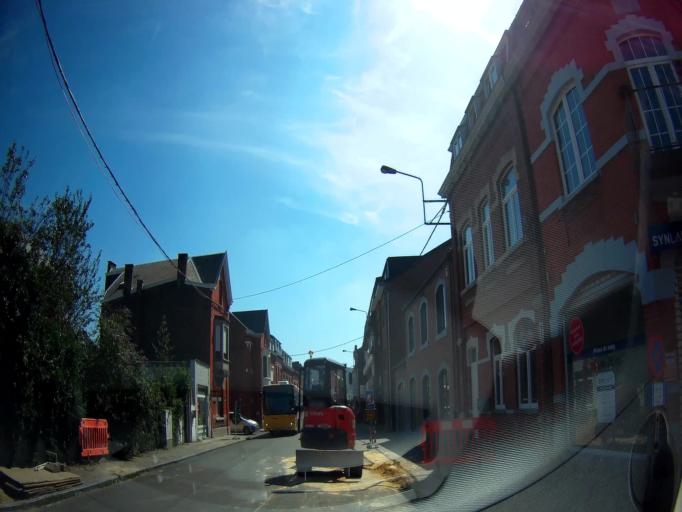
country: BE
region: Wallonia
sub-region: Province de Liege
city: Amay
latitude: 50.5476
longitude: 5.3196
